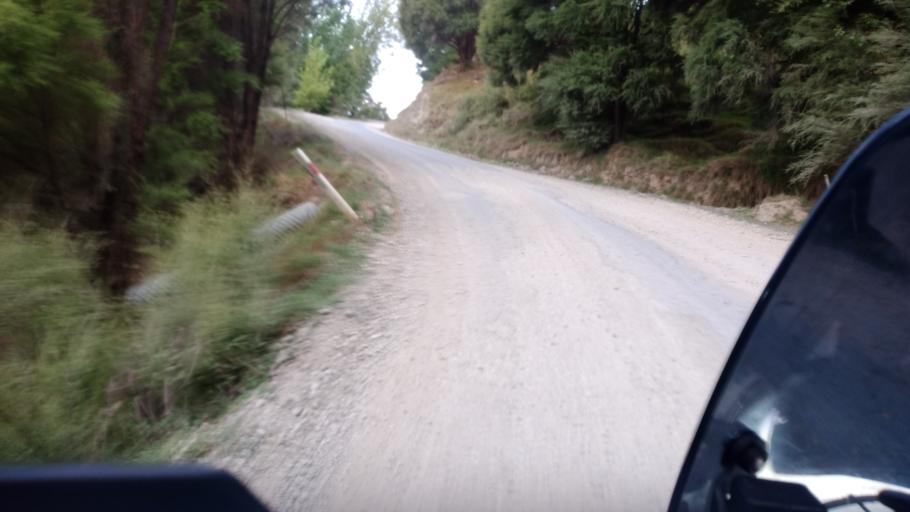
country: NZ
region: Gisborne
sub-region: Gisborne District
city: Gisborne
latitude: -38.4773
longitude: 177.9734
